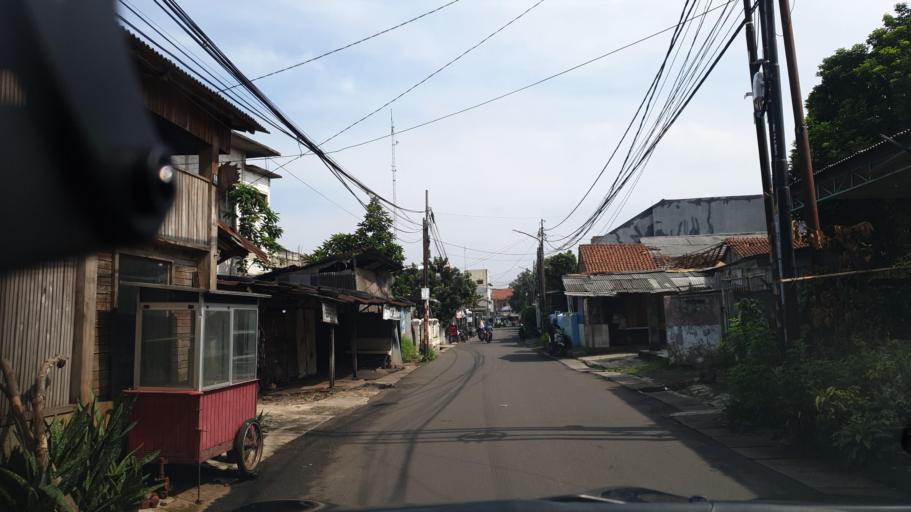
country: ID
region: West Java
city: Pamulang
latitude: -6.3049
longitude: 106.7656
